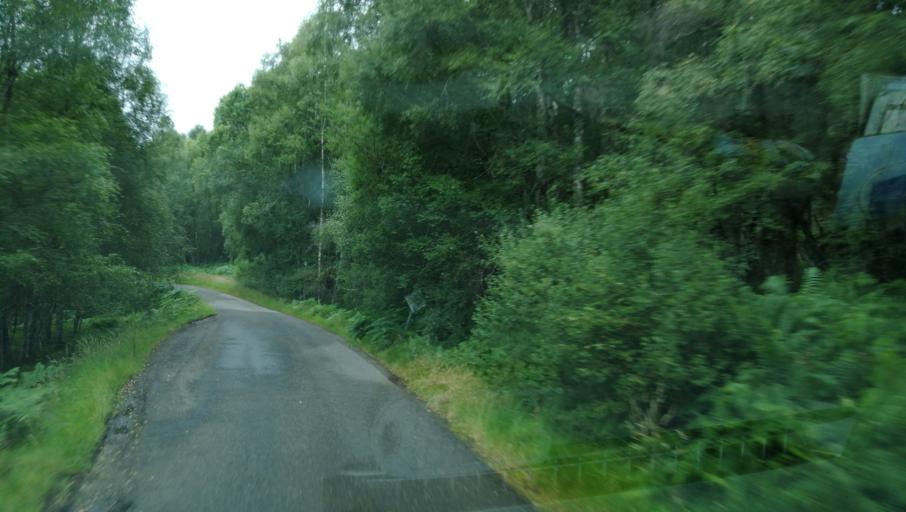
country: GB
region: Scotland
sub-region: Highland
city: Spean Bridge
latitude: 57.3125
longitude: -4.8582
